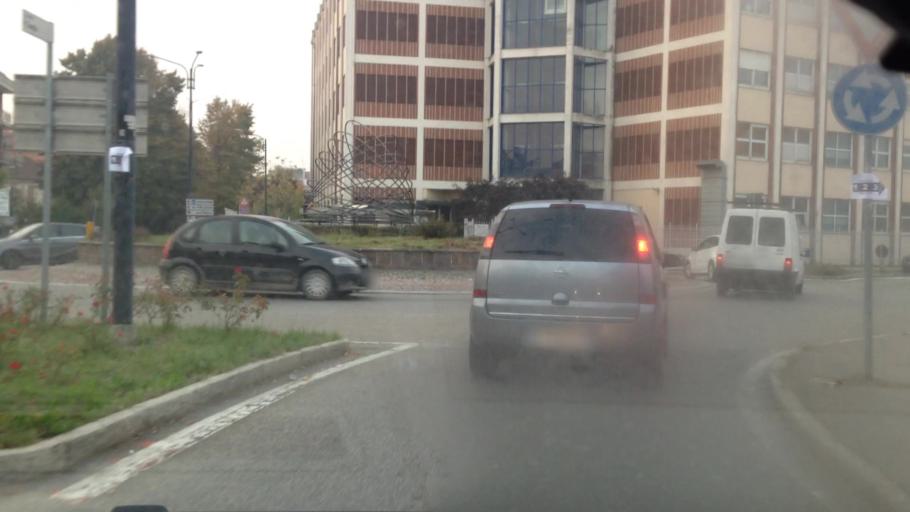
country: IT
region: Piedmont
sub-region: Provincia di Asti
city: Asti
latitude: 44.9114
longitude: 8.1977
